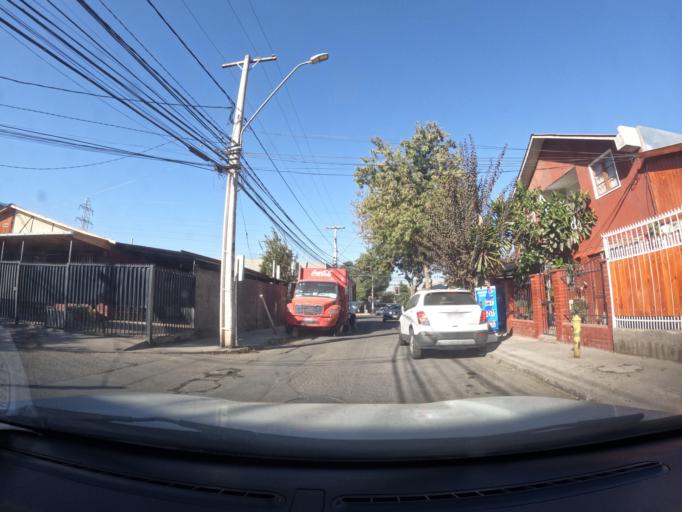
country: CL
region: Santiago Metropolitan
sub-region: Provincia de Santiago
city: Villa Presidente Frei, Nunoa, Santiago, Chile
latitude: -33.5006
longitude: -70.5824
